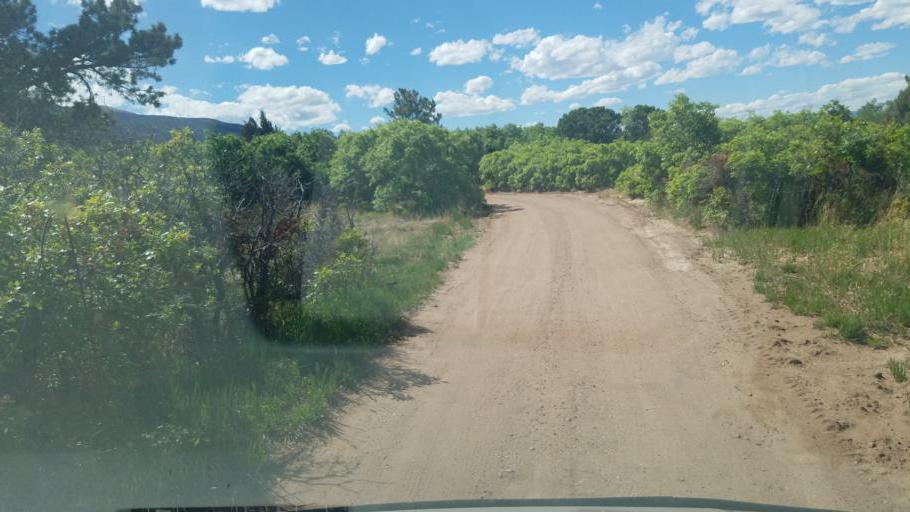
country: US
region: Colorado
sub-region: Custer County
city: Westcliffe
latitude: 38.2215
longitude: -105.6043
